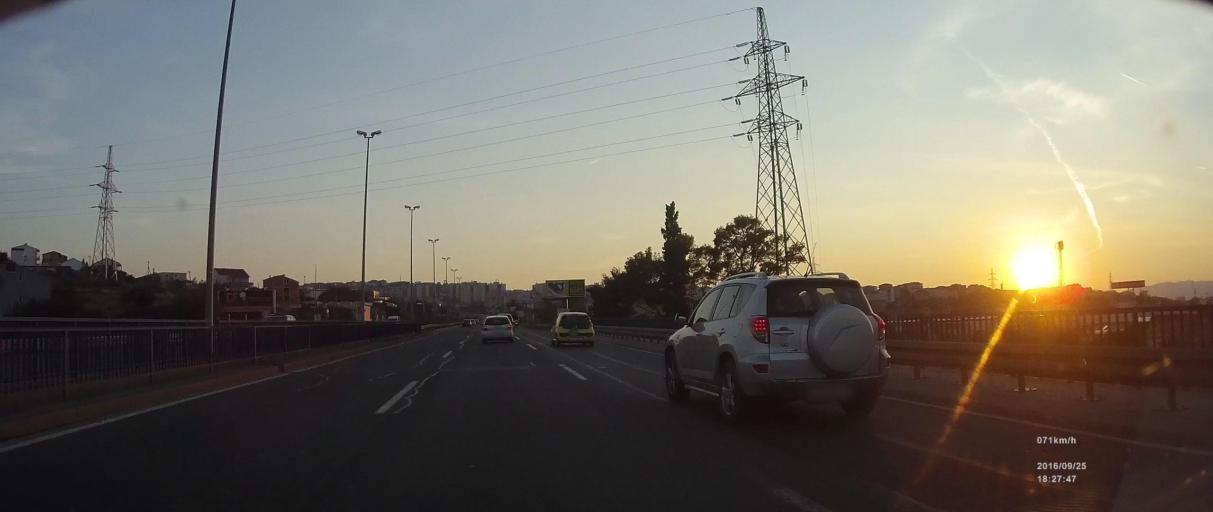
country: HR
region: Splitsko-Dalmatinska
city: Solin
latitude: 43.5249
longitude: 16.4886
